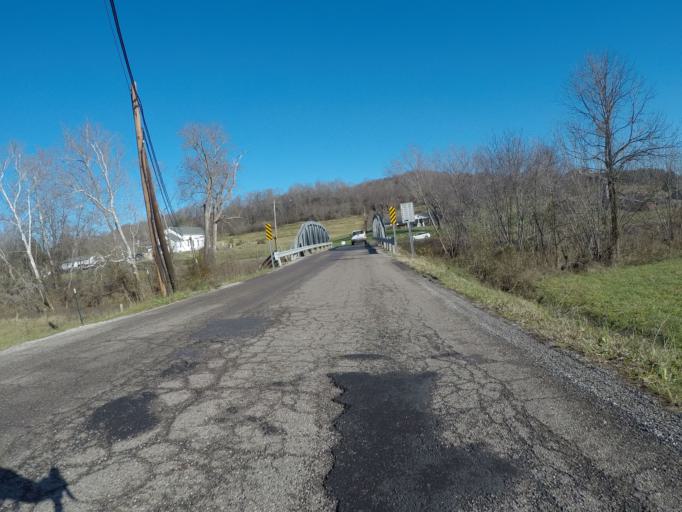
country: US
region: West Virginia
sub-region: Cabell County
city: Huntington
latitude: 38.4856
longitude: -82.4689
